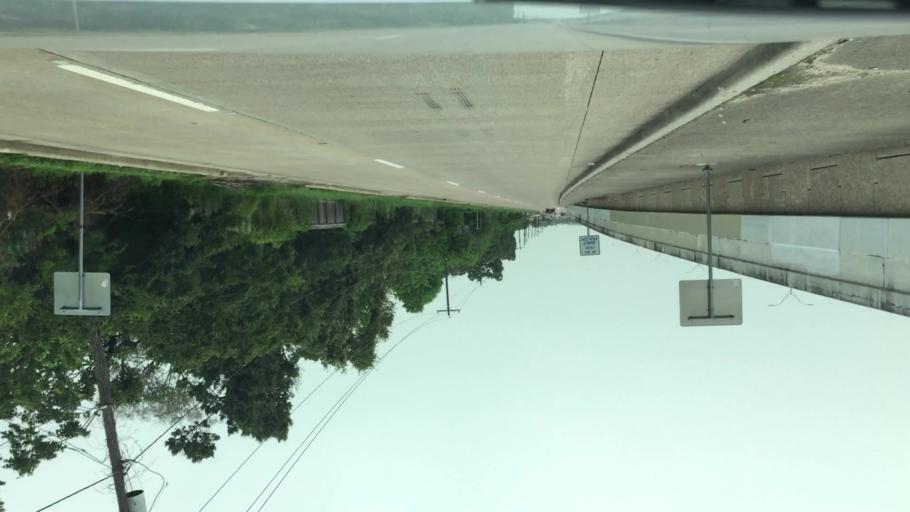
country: US
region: Texas
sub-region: Harris County
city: Cloverleaf
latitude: 29.7857
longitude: -95.1588
